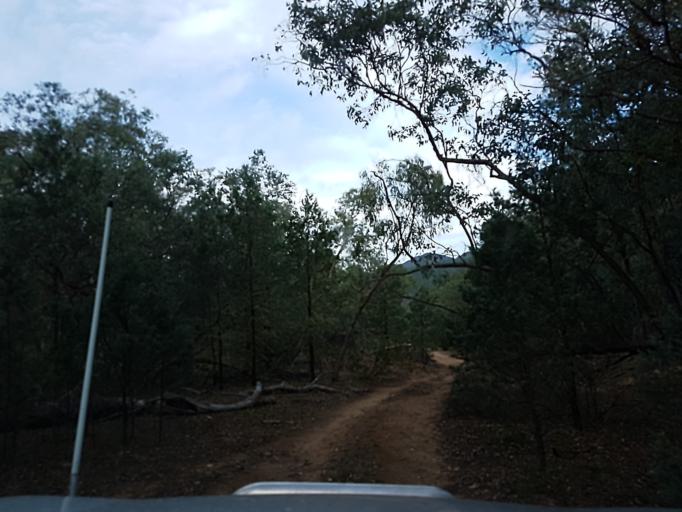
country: AU
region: New South Wales
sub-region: Snowy River
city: Jindabyne
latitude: -36.9441
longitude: 148.3899
